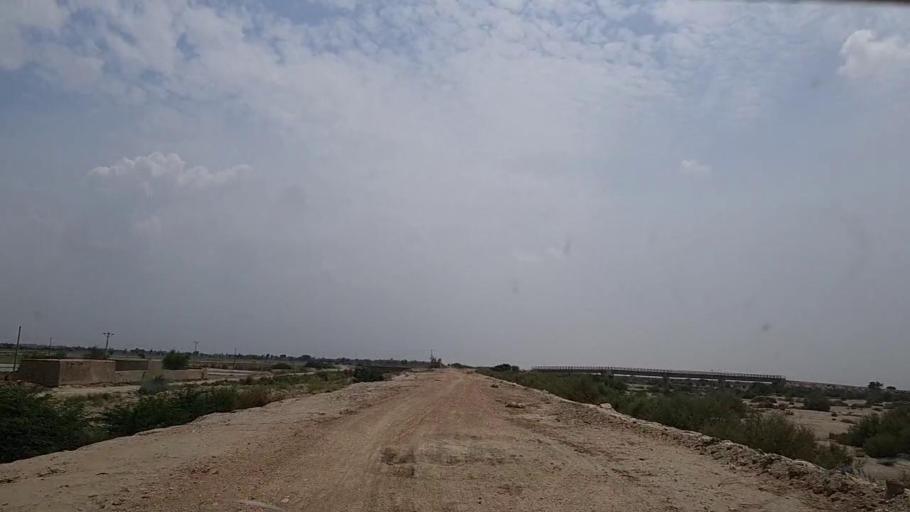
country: PK
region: Sindh
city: Phulji
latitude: 26.8235
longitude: 67.6136
